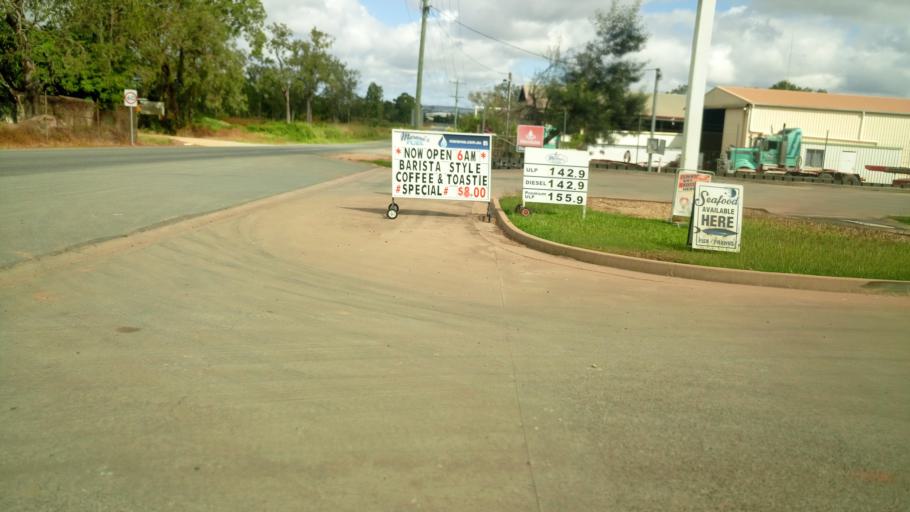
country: AU
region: Queensland
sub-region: Tablelands
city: Mareeba
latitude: -16.9735
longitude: 145.4132
